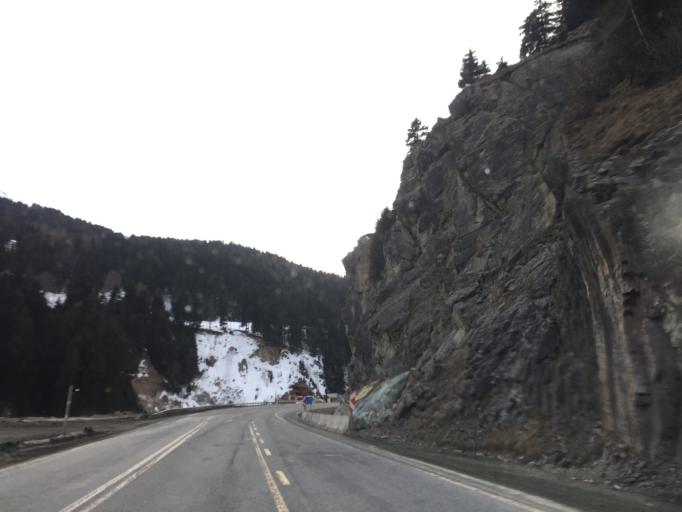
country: TR
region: Gumushane
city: Yaglidere
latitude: 40.6759
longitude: 39.4315
